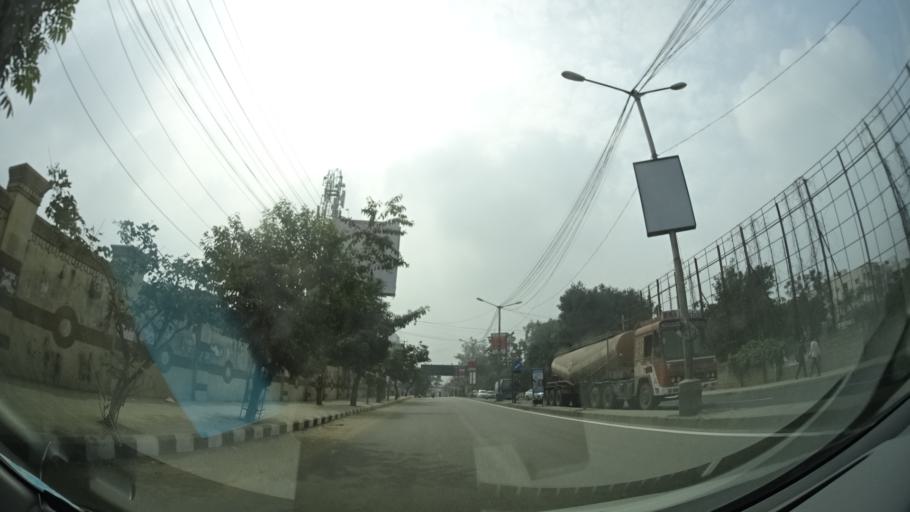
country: IN
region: Karnataka
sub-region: Bangalore Rural
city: Hoskote
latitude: 12.9822
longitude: 77.7522
